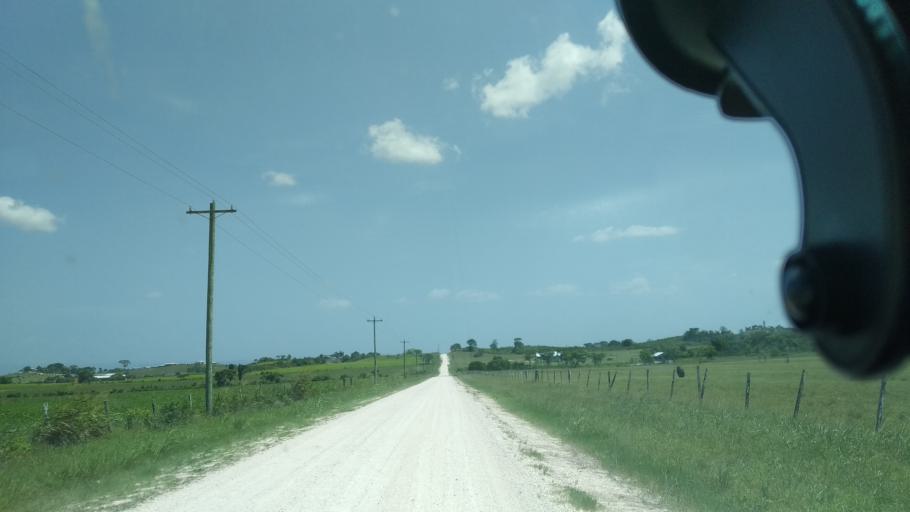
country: BZ
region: Cayo
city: San Ignacio
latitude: 17.3139
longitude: -89.0479
